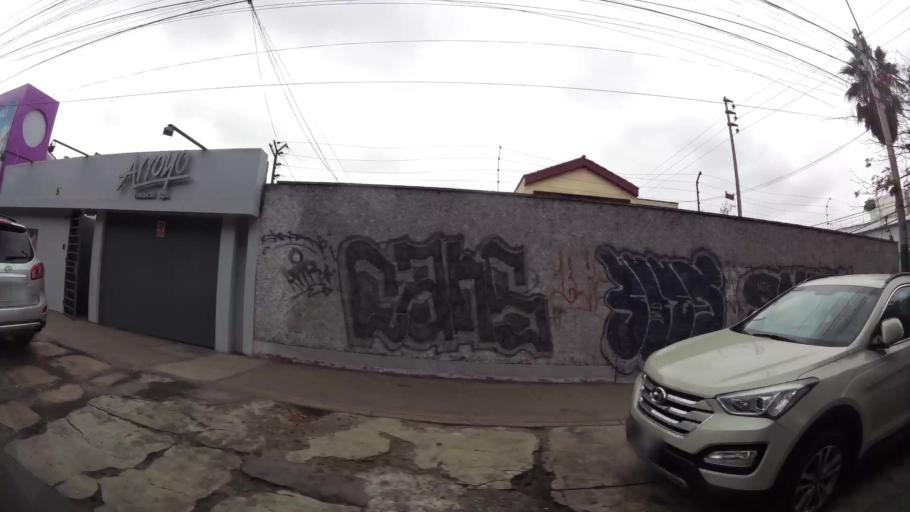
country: PE
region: Lima
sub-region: Lima
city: Surco
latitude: -12.1239
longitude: -76.9845
